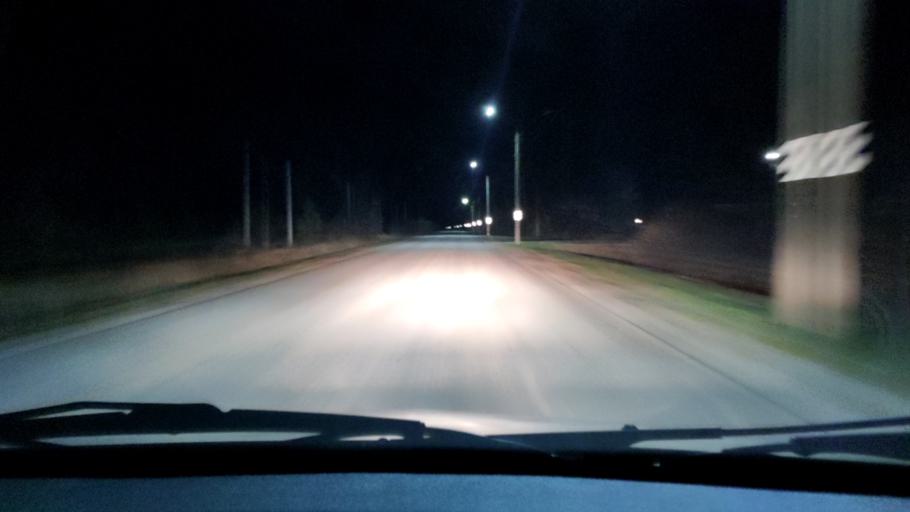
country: RU
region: Voronezj
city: Novaya Usman'
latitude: 51.6558
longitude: 39.4412
